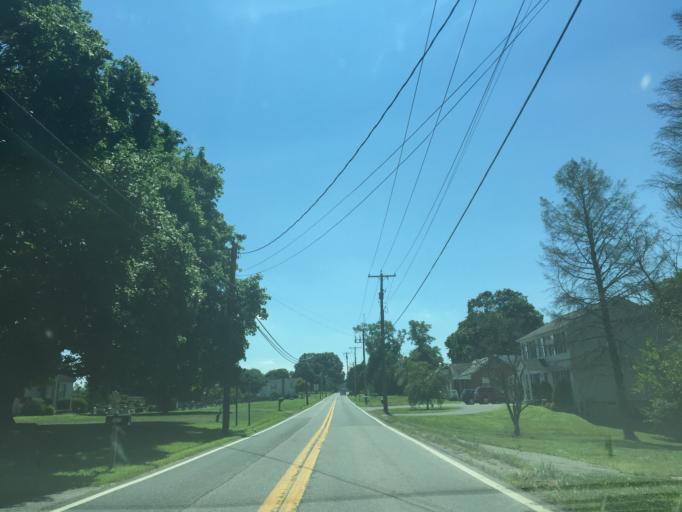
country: US
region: Maryland
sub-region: Harford County
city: Bel Air North
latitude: 39.5971
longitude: -76.3909
